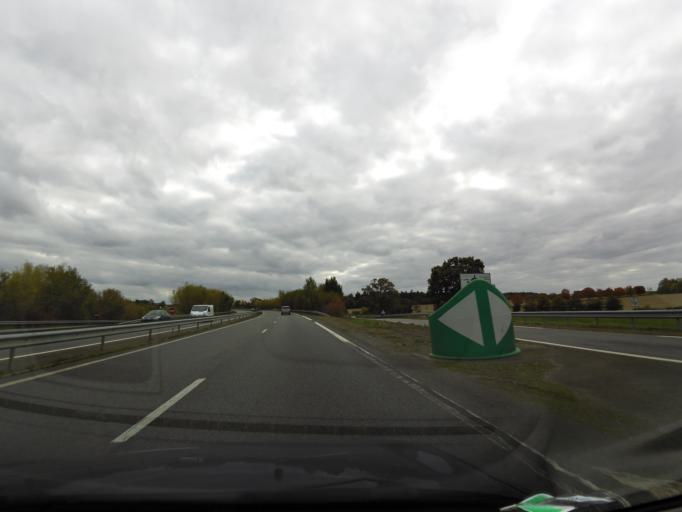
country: FR
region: Brittany
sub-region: Departement d'Ille-et-Vilaine
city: Saint-Armel
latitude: 48.0169
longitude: -1.6020
